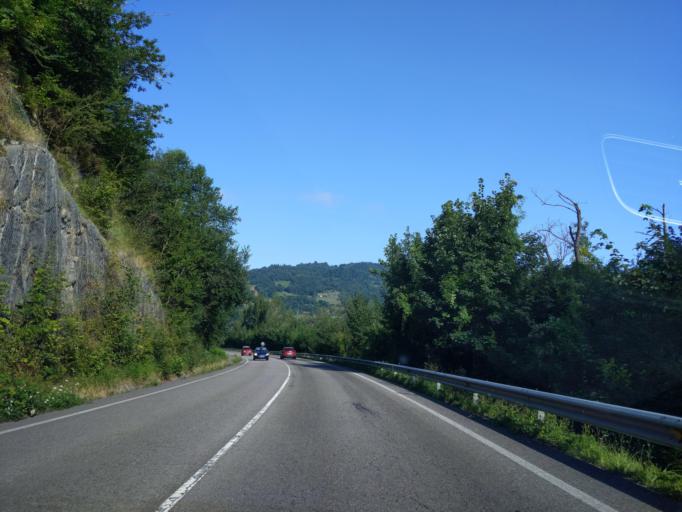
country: ES
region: Asturias
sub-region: Province of Asturias
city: Pola de Laviana
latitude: 43.2334
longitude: -5.4959
